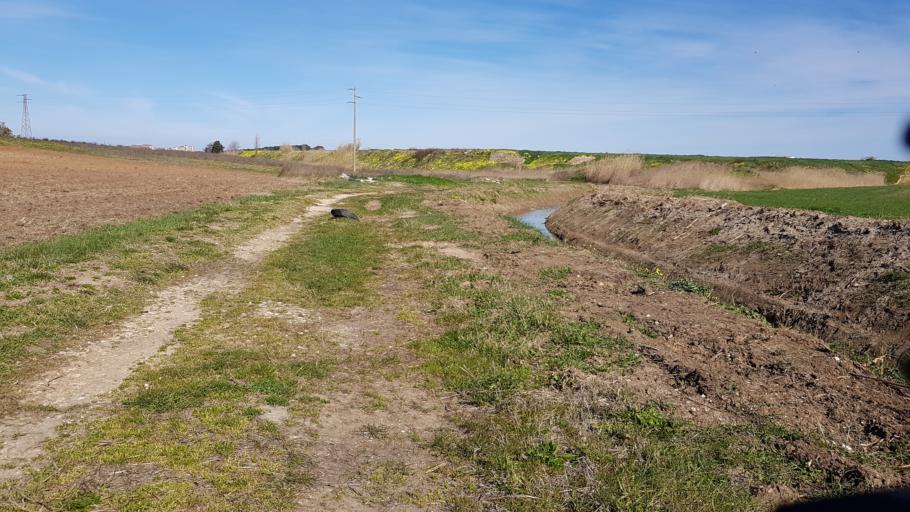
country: IT
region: Apulia
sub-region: Provincia di Brindisi
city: La Rosa
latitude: 40.6043
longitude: 17.9333
